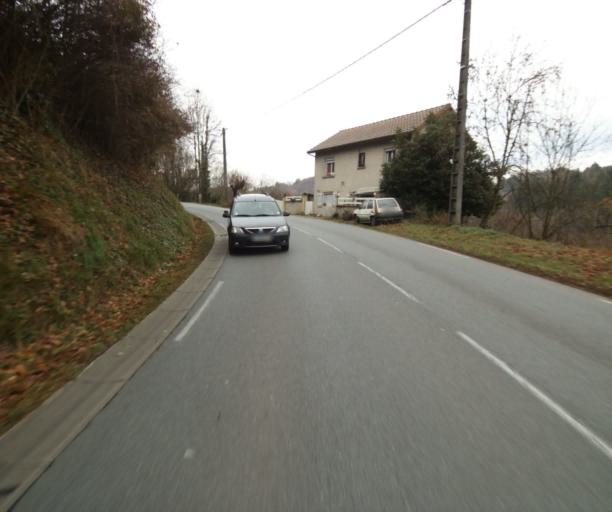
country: FR
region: Limousin
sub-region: Departement de la Correze
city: Tulle
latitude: 45.2666
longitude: 1.7433
